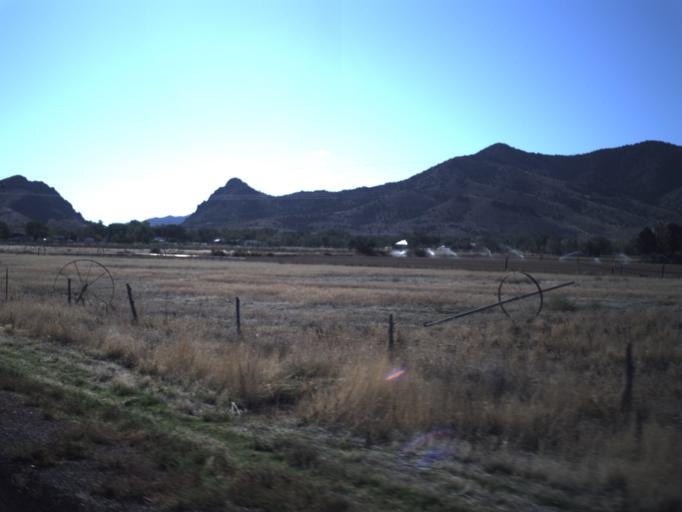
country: US
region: Utah
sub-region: Washington County
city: Enterprise
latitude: 37.6732
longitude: -113.5554
